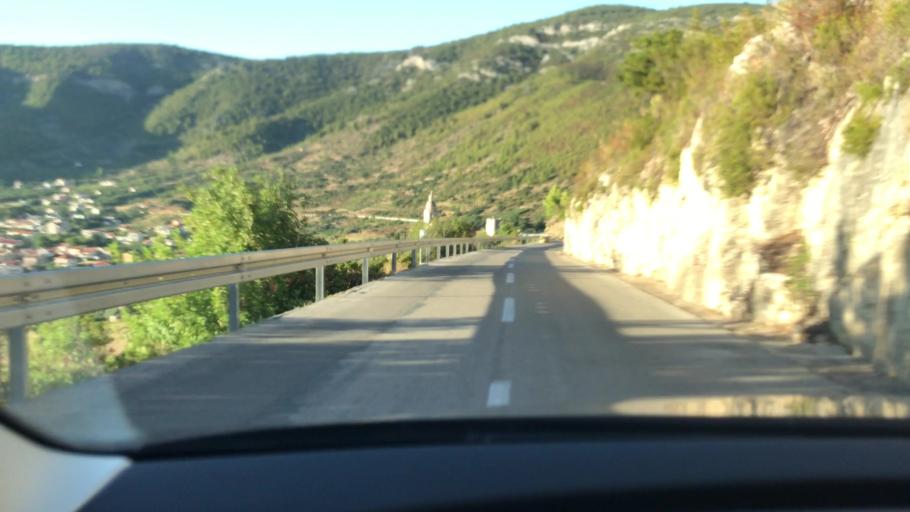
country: HR
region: Splitsko-Dalmatinska
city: Komiza
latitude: 43.0368
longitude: 16.0951
